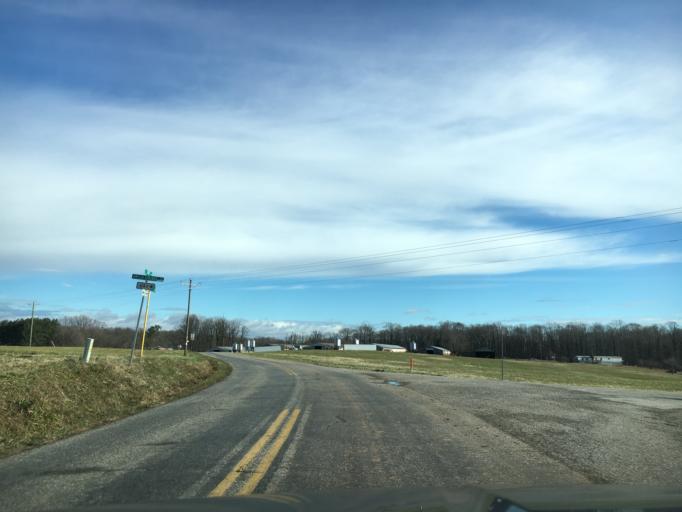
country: US
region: Virginia
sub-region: Amelia County
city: Amelia Court House
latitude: 37.3809
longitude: -78.1284
